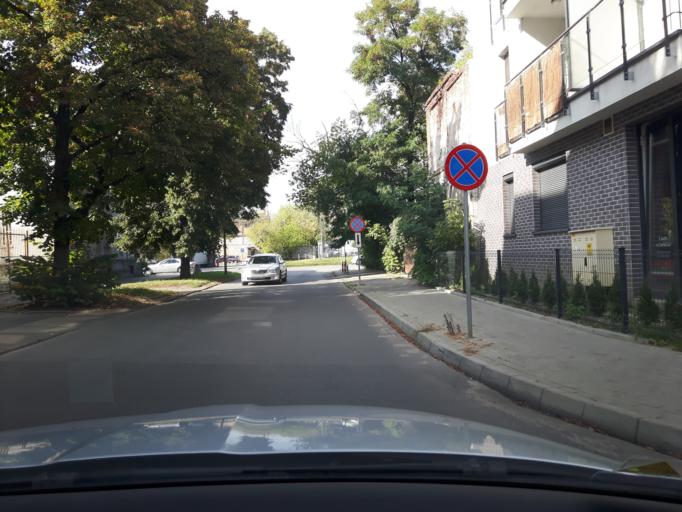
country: PL
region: Masovian Voivodeship
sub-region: Warszawa
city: Praga Poludnie
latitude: 52.2490
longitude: 21.0635
